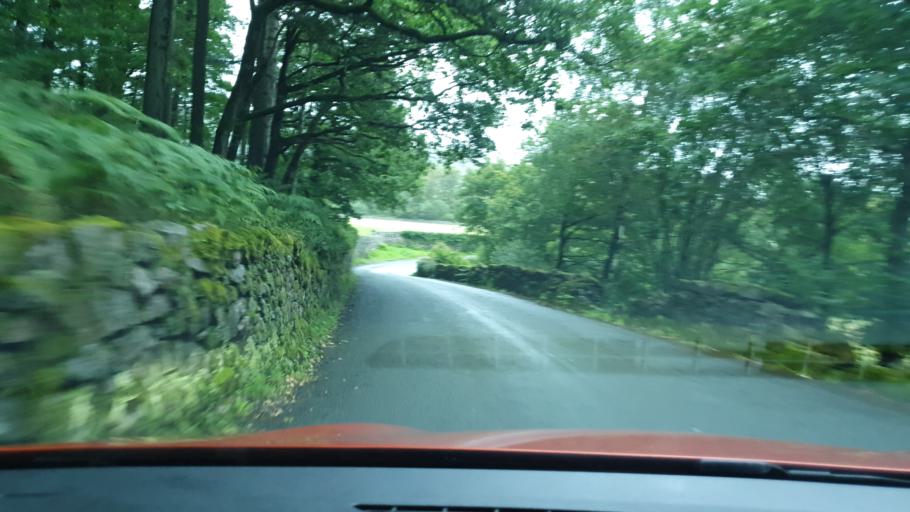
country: GB
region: England
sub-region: Cumbria
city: Seascale
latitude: 54.3868
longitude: -3.3142
